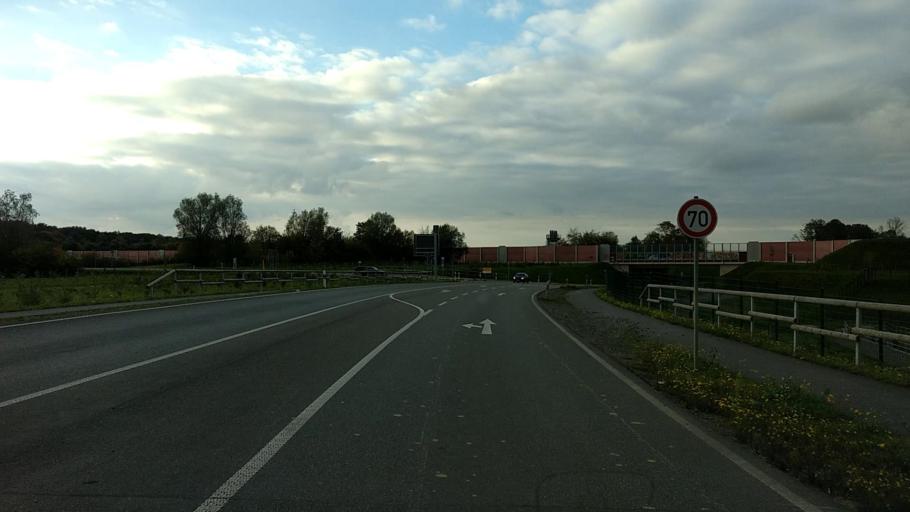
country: DE
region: North Rhine-Westphalia
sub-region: Regierungsbezirk Koln
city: Kerpen
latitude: 50.8914
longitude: 6.6437
